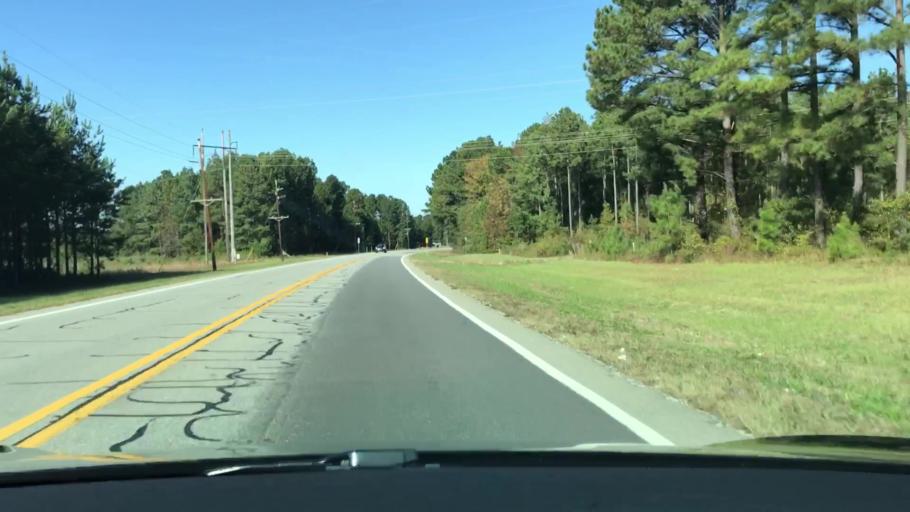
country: US
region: Georgia
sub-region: Warren County
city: Warrenton
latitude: 33.3902
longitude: -82.6449
